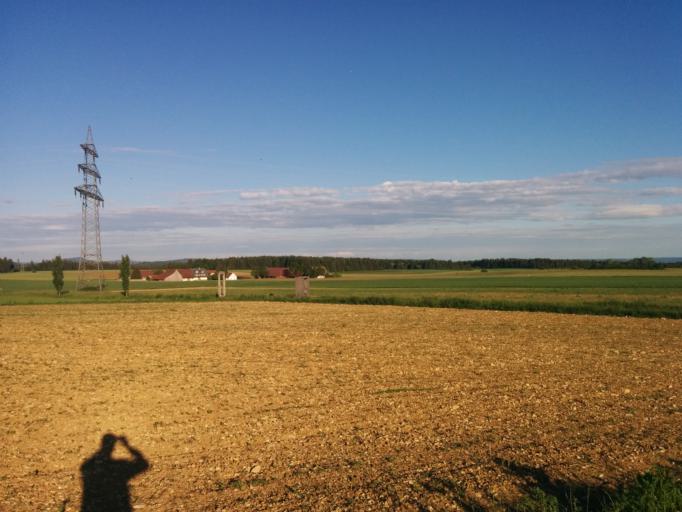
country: DE
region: Baden-Wuerttemberg
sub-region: Freiburg Region
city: Villingen-Schwenningen
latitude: 48.0561
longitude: 8.4810
